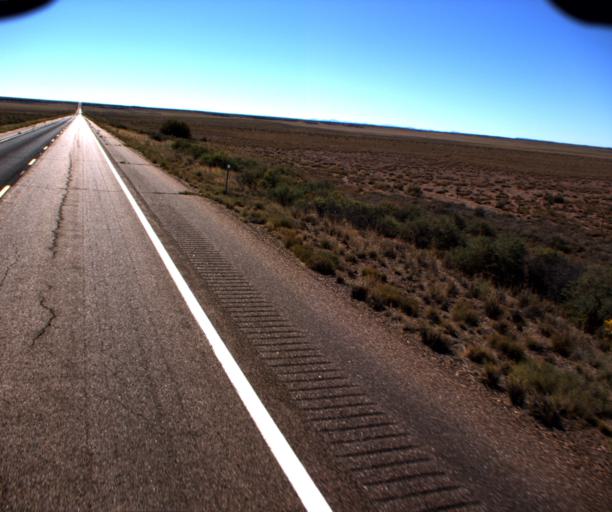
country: US
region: Arizona
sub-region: Navajo County
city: Snowflake
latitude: 34.7426
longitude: -109.7940
